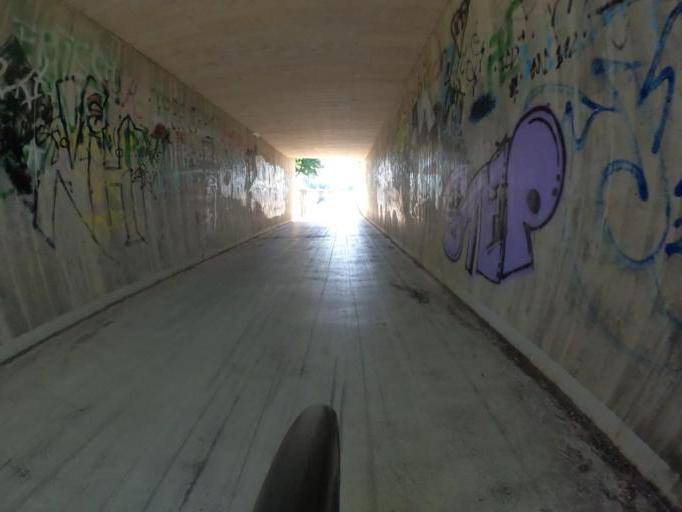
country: DE
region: Baden-Wuerttemberg
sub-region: Karlsruhe Region
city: Mauer
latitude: 49.3422
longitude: 8.7893
